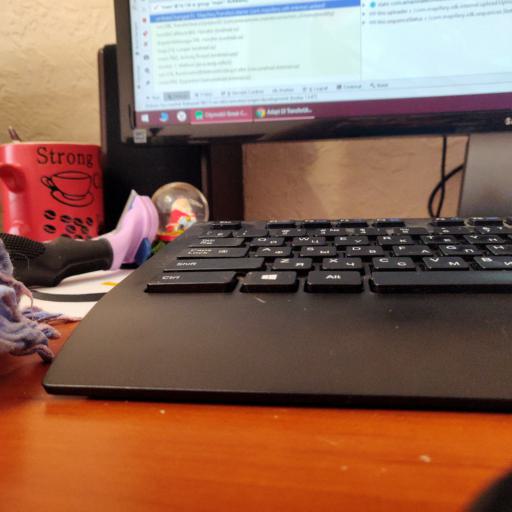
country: FI
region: Haeme
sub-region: Forssa
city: Humppila
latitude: 60.8842
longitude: 23.4322
